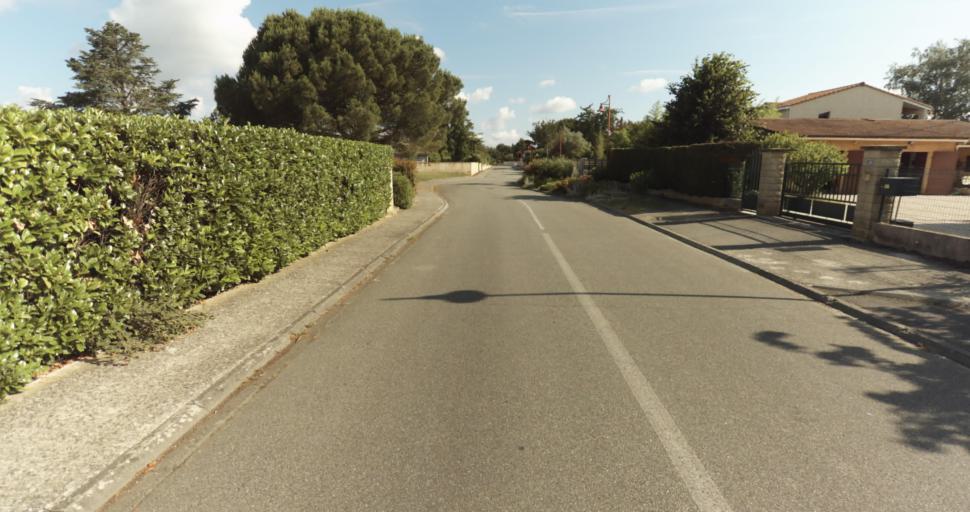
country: FR
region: Midi-Pyrenees
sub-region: Departement de la Haute-Garonne
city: Fontenilles
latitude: 43.5639
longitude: 1.2060
